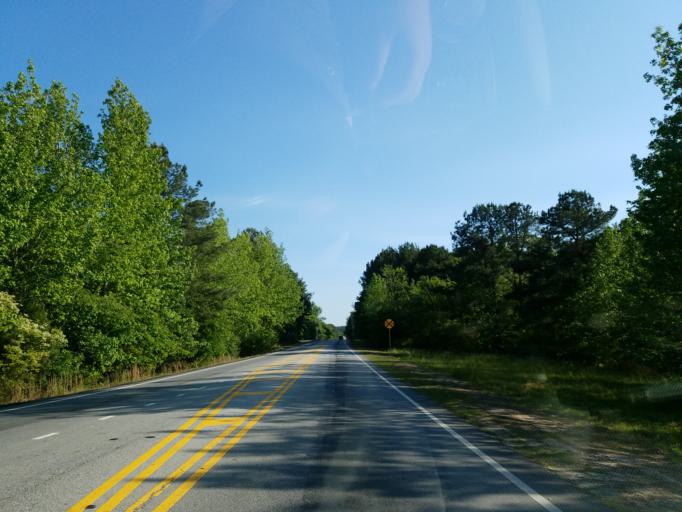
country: US
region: Georgia
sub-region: Carroll County
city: Villa Rica
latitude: 33.7410
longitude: -84.9371
